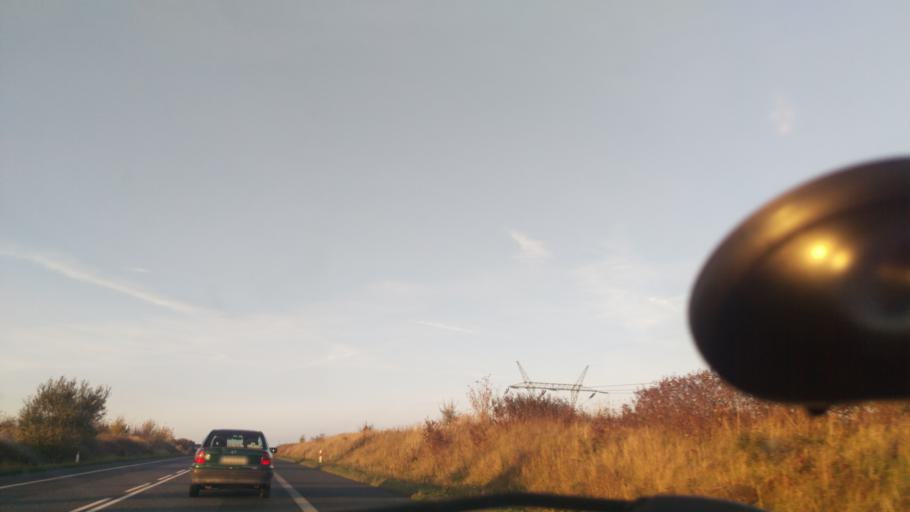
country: PL
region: West Pomeranian Voivodeship
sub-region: Powiat gryfinski
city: Stare Czarnowo
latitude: 53.2902
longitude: 14.7885
